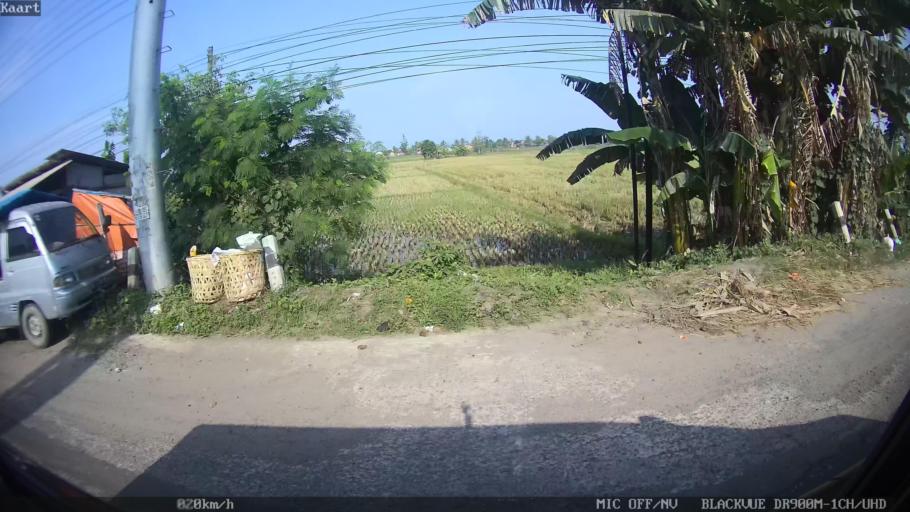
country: ID
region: Lampung
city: Natar
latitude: -5.3010
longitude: 105.1918
